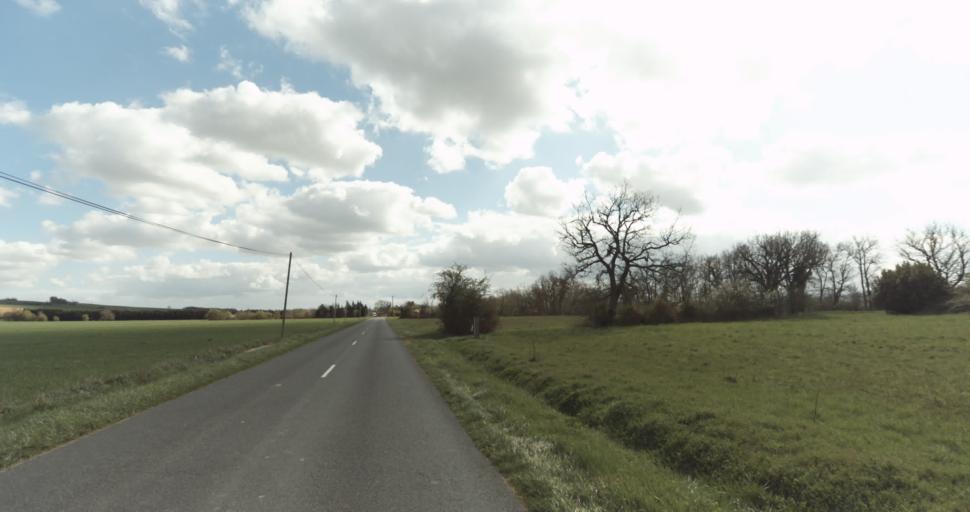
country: FR
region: Midi-Pyrenees
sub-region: Departement de la Haute-Garonne
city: Auterive
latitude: 43.3859
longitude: 1.4590
